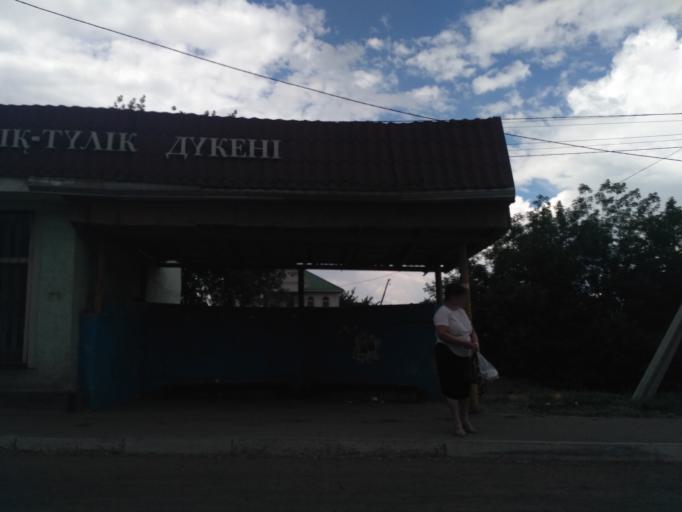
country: KZ
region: Almaty Oblysy
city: Burunday
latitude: 43.2072
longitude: 76.6378
